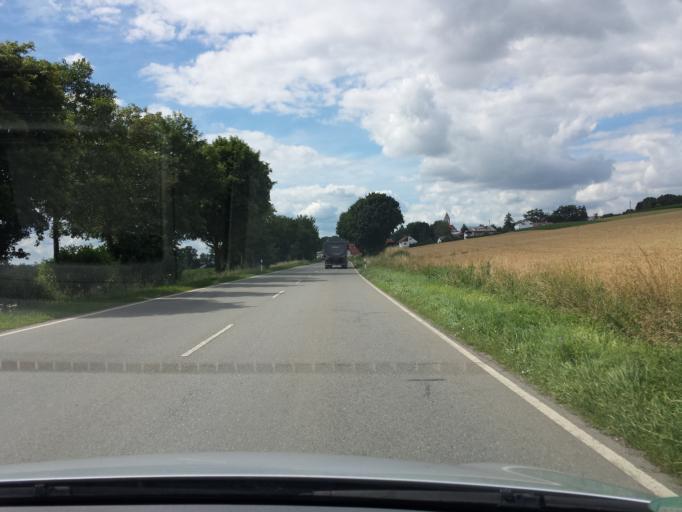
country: DE
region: Baden-Wuerttemberg
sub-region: Tuebingen Region
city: Burgrieden
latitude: 48.2334
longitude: 9.9422
